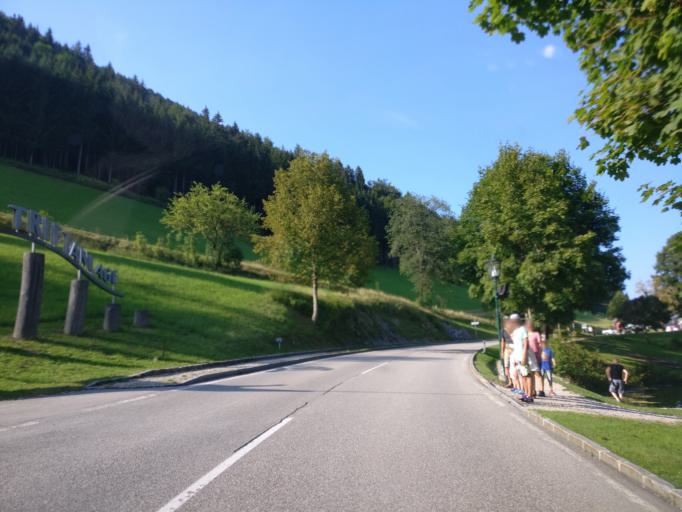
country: AT
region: Lower Austria
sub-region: Politischer Bezirk Scheibbs
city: Gostling an der Ybbs
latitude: 47.7426
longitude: 14.8916
